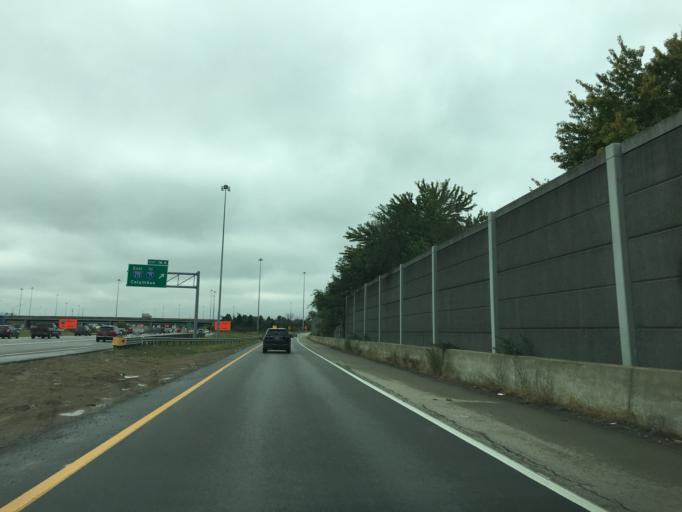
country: US
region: Ohio
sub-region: Hamilton County
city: Glendale
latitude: 39.2965
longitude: -84.4414
